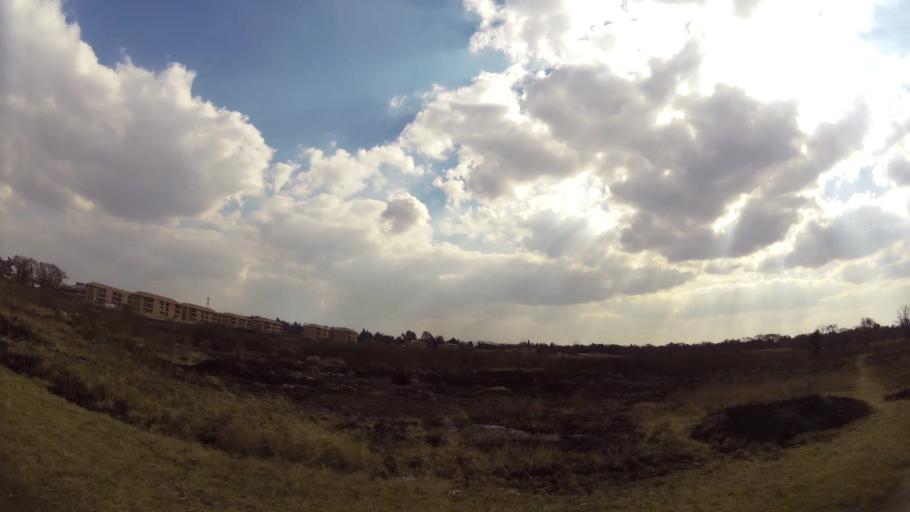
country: ZA
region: Mpumalanga
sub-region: Nkangala District Municipality
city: Delmas
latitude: -26.1467
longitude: 28.6794
